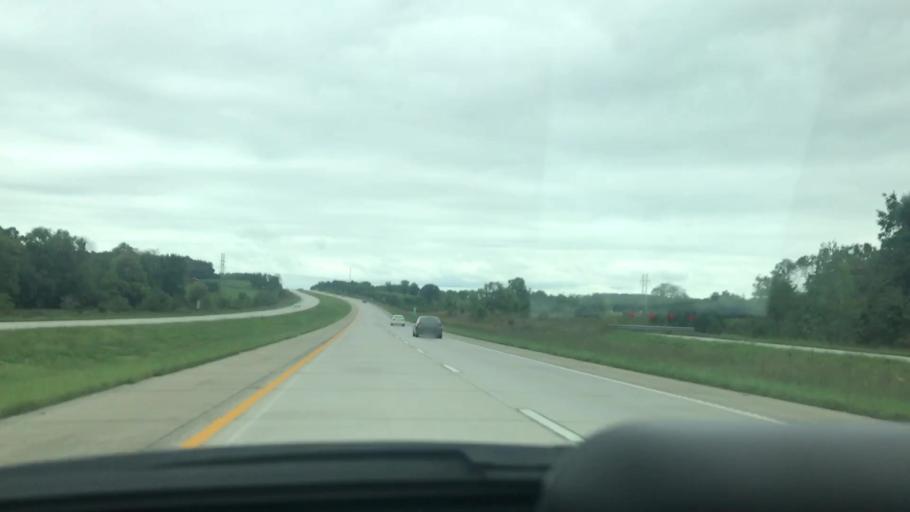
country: US
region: Missouri
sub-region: Dallas County
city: Buffalo
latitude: 37.5279
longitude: -93.1375
